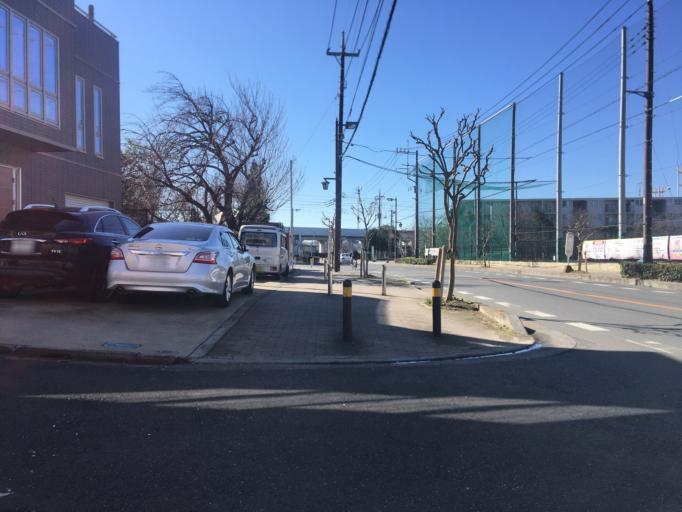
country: JP
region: Saitama
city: Shiki
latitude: 35.8066
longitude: 139.5701
